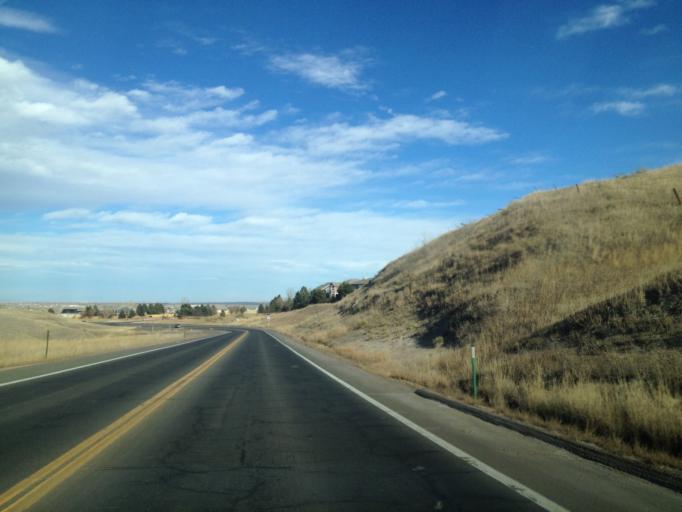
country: US
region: Colorado
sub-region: Boulder County
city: Superior
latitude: 39.9142
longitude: -105.1660
